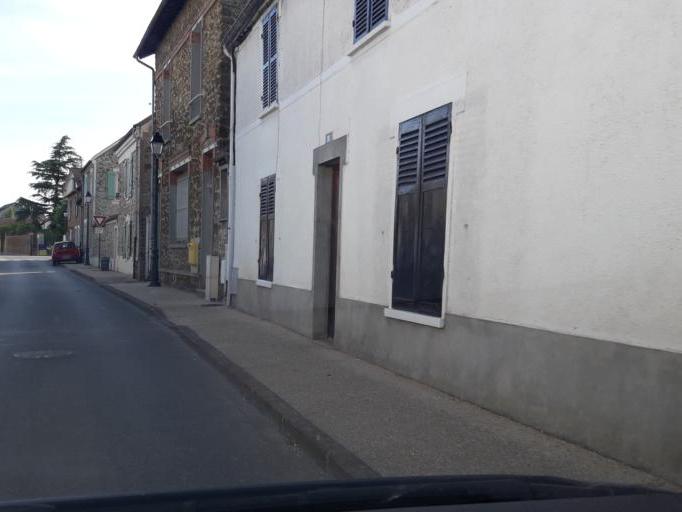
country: FR
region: Ile-de-France
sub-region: Departement de l'Essonne
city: Vert-le-Grand
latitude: 48.5714
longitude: 2.3598
